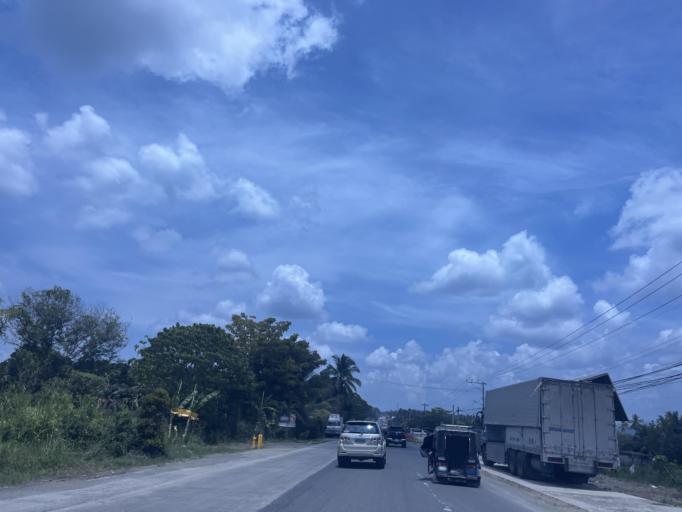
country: PH
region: Davao
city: Lacson
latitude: 7.1961
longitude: 125.4505
